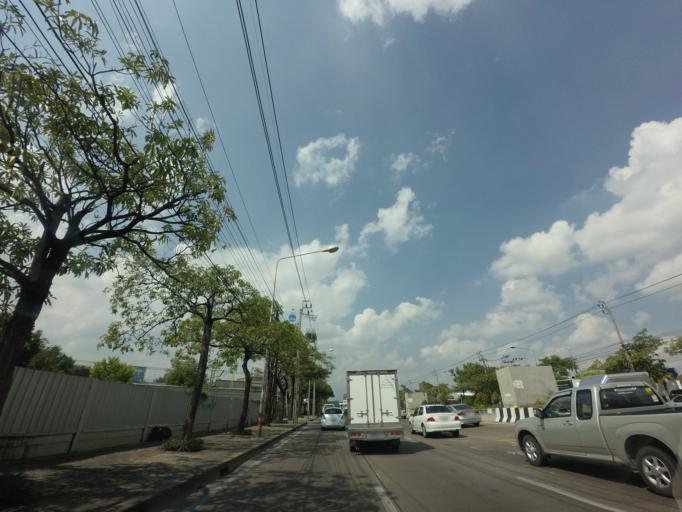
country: TH
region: Bangkok
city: Lat Phrao
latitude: 13.8395
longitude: 100.5990
